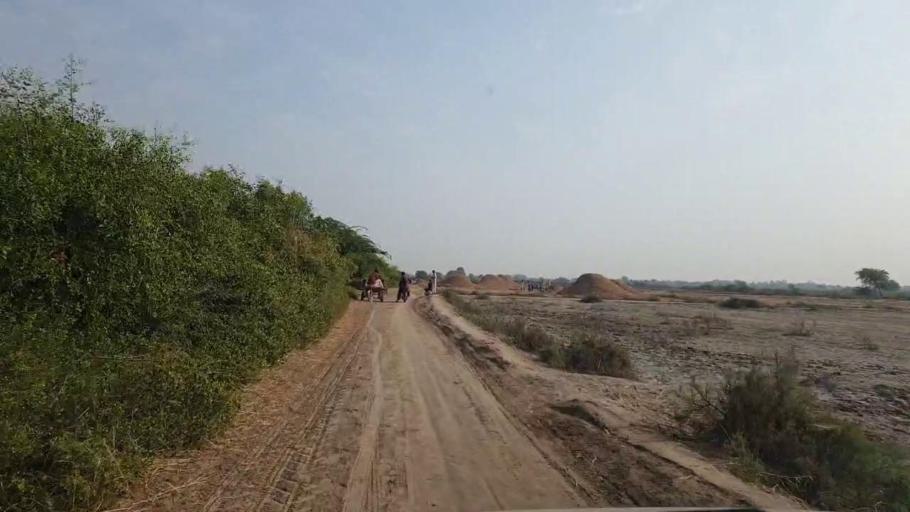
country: PK
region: Sindh
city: Talhar
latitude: 24.8973
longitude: 68.8886
